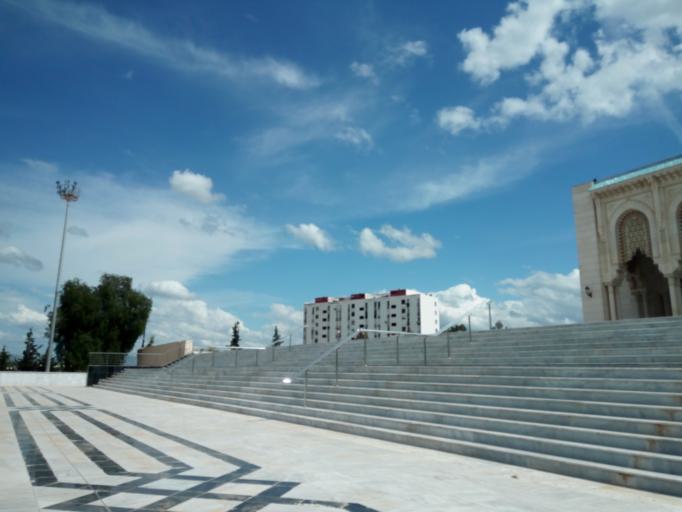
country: DZ
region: Constantine
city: Constantine
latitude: 36.3481
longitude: 6.6036
